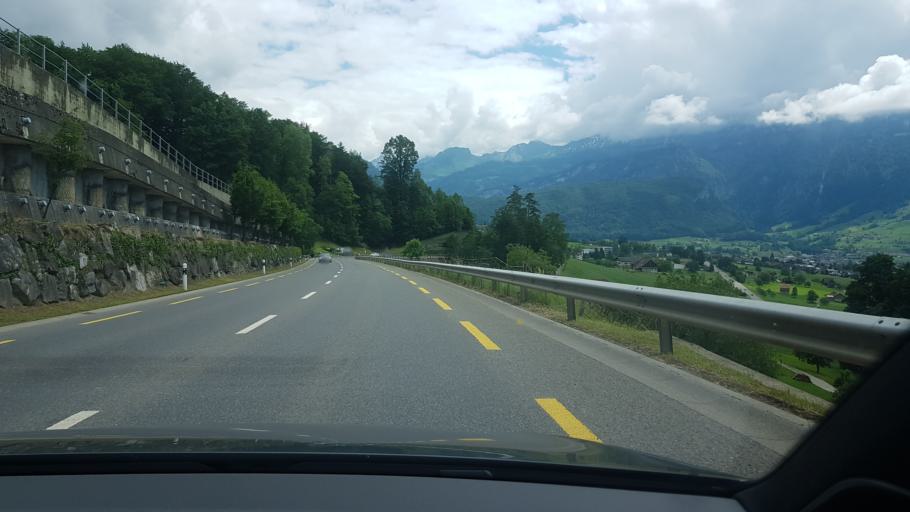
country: CH
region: Schwyz
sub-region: Bezirk Schwyz
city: Schwyz
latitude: 47.0412
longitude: 8.6382
